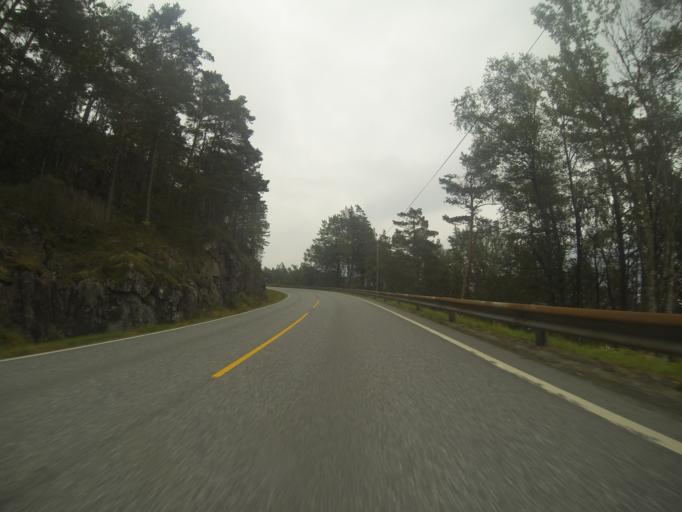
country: NO
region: Rogaland
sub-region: Suldal
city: Sand
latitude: 59.5206
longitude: 6.2439
